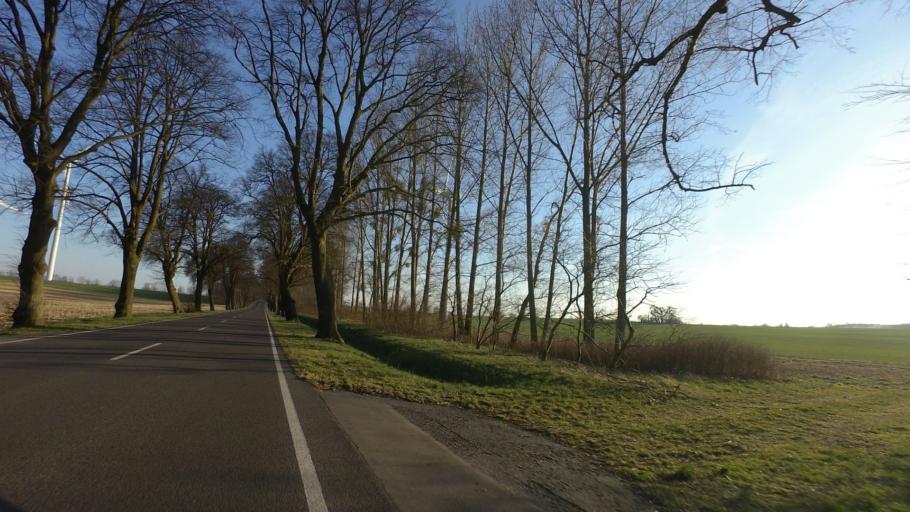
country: DE
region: Brandenburg
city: Werftpfuhl
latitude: 52.7078
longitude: 13.8368
